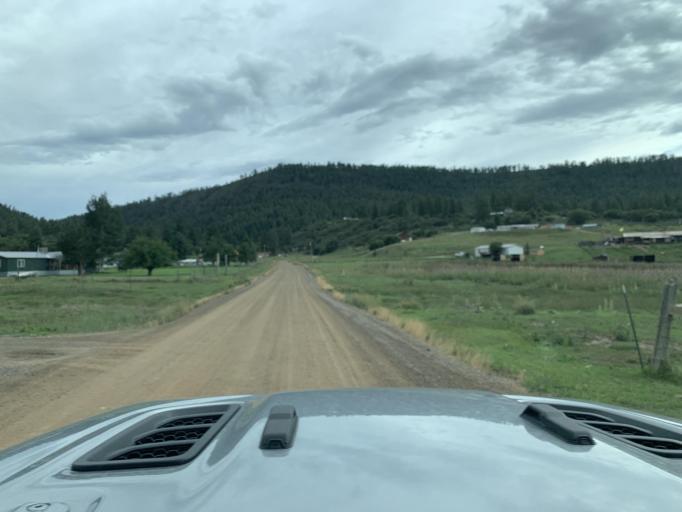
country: US
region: Colorado
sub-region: Archuleta County
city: Pagosa Springs
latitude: 37.2204
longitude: -107.1886
